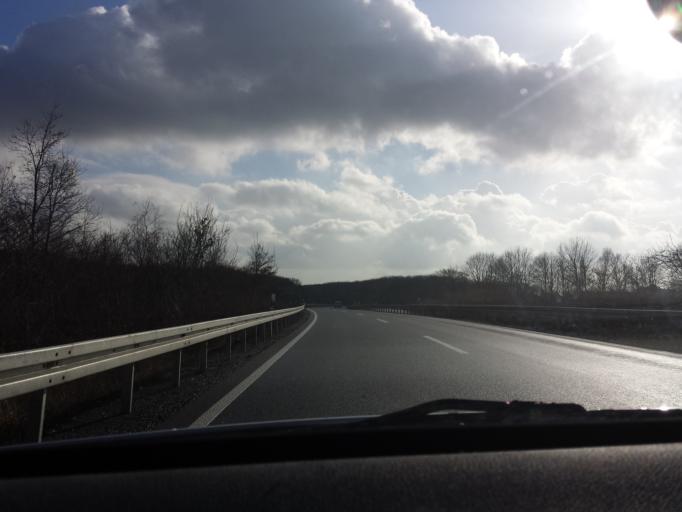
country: DE
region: North Rhine-Westphalia
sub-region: Regierungsbezirk Dusseldorf
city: Erkrath
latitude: 51.1887
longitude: 6.8706
